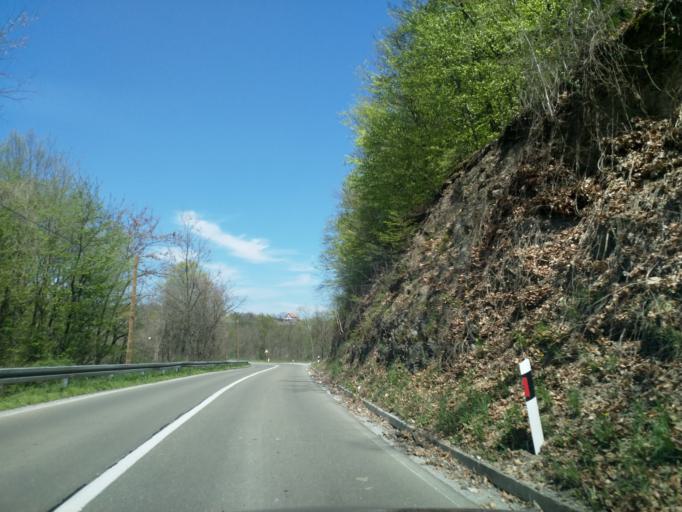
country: RS
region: Central Serbia
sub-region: Belgrade
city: Lazarevac
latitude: 44.3591
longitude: 20.3514
